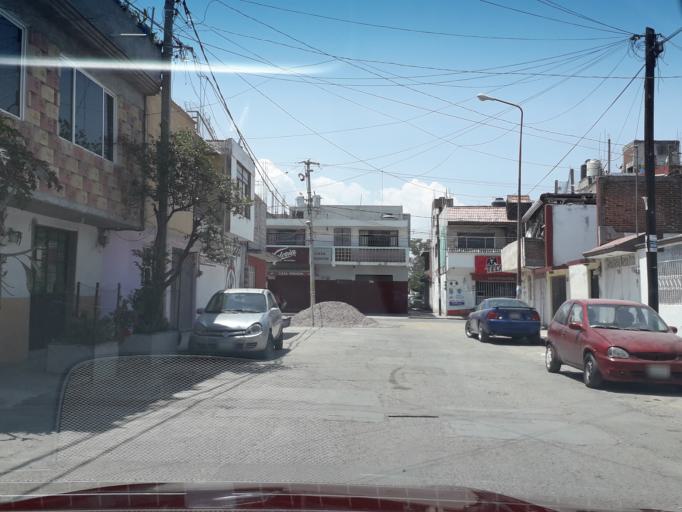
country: MX
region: Puebla
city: Tlazcalancingo
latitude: 18.9988
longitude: -98.2378
